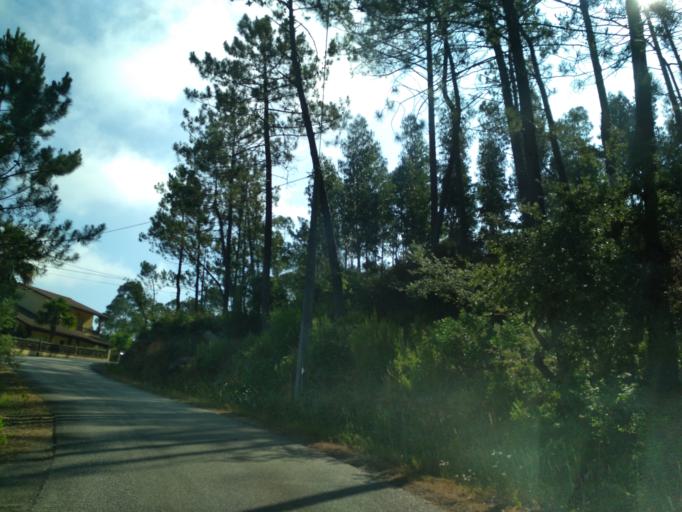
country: PT
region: Coimbra
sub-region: Soure
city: Soure
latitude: 39.9933
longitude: -8.5767
